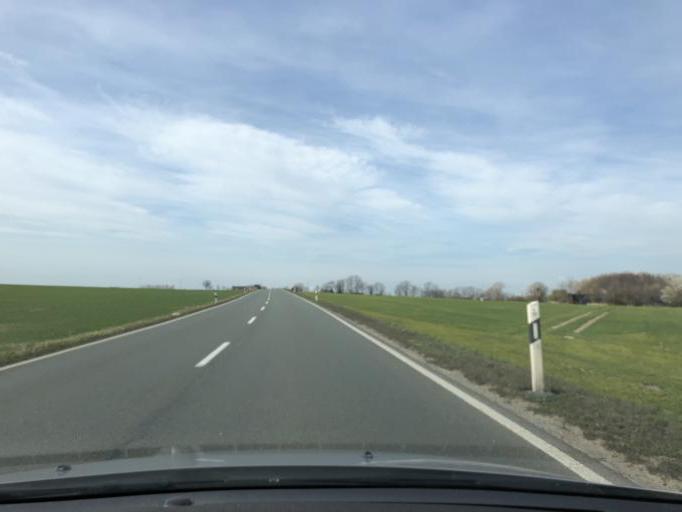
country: DE
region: Saxony-Anhalt
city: Osterfeld
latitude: 51.0820
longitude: 11.9792
